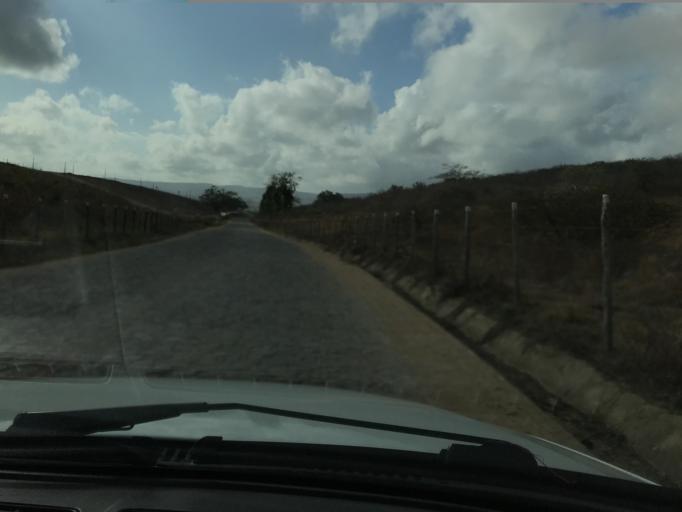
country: BR
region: Pernambuco
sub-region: Bezerros
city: Bezerros
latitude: -8.2134
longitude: -35.7553
